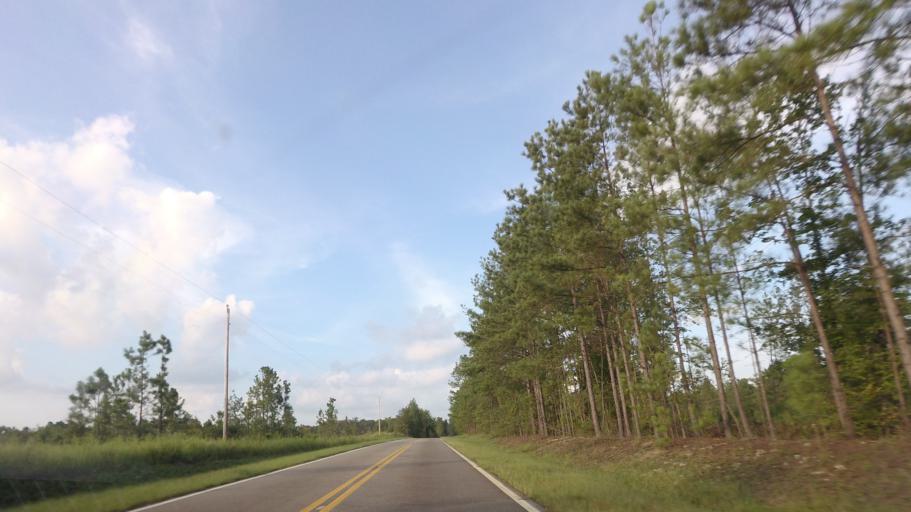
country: US
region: Georgia
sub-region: Wilkinson County
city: Gordon
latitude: 32.8329
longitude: -83.4137
